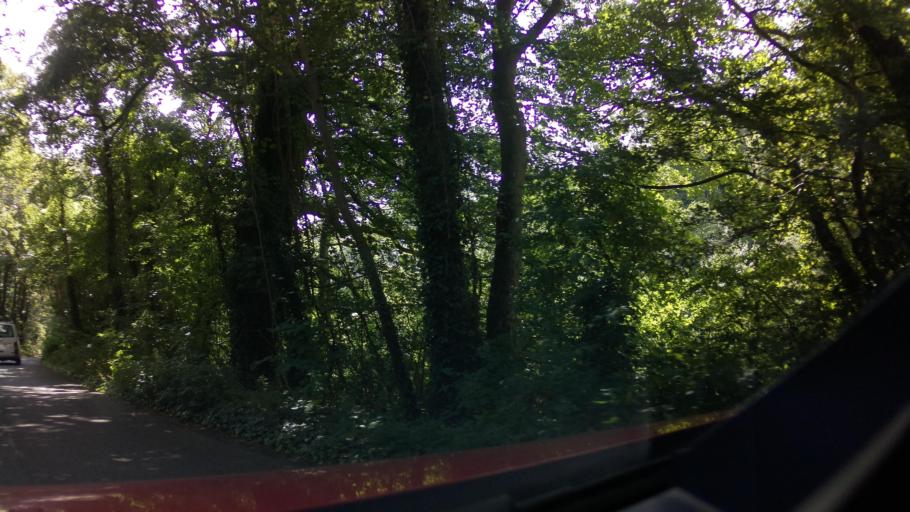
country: GB
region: England
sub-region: Devon
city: Dartmouth
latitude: 50.3560
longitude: -3.5629
